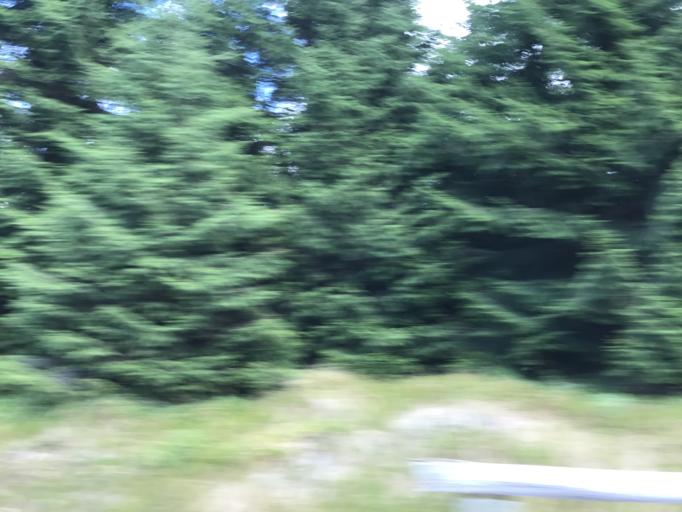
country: DE
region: Lower Saxony
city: Sankt Andreasberg
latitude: 51.7490
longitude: 10.5215
